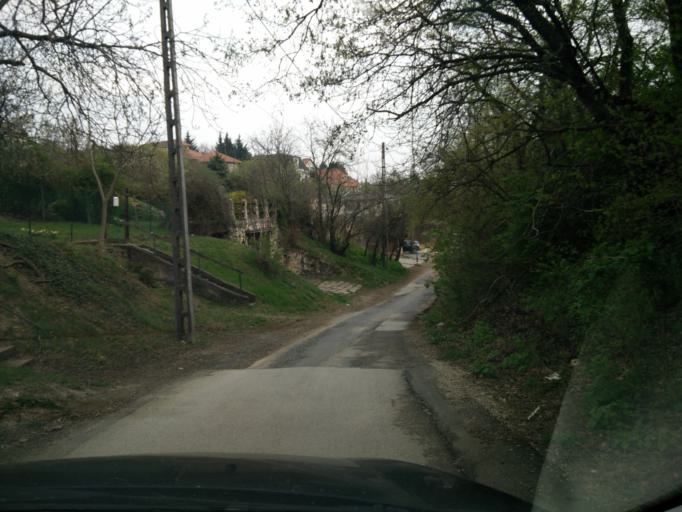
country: HU
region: Pest
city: Budaors
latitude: 47.4703
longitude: 18.9534
